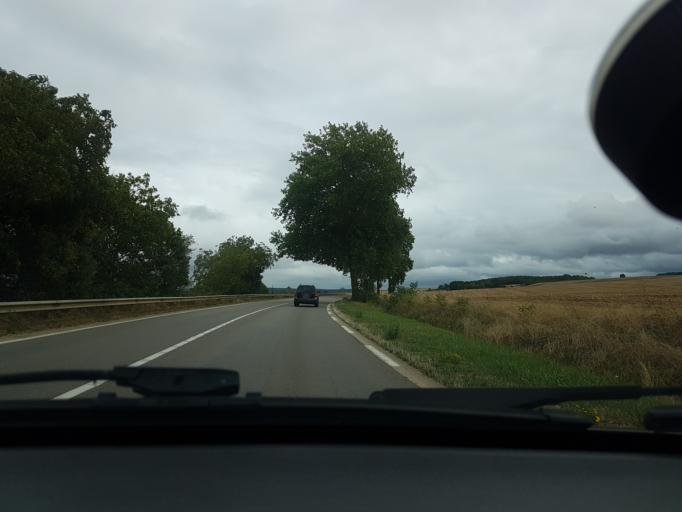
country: FR
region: Bourgogne
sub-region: Departement de l'Yonne
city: Saint-Bris-le-Vineux
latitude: 47.6934
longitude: 3.6443
